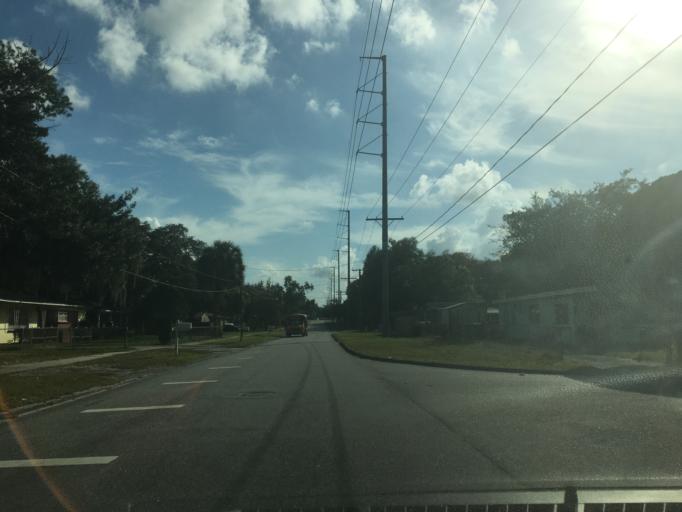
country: US
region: Florida
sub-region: Hillsborough County
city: University
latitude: 28.0356
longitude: -82.4305
